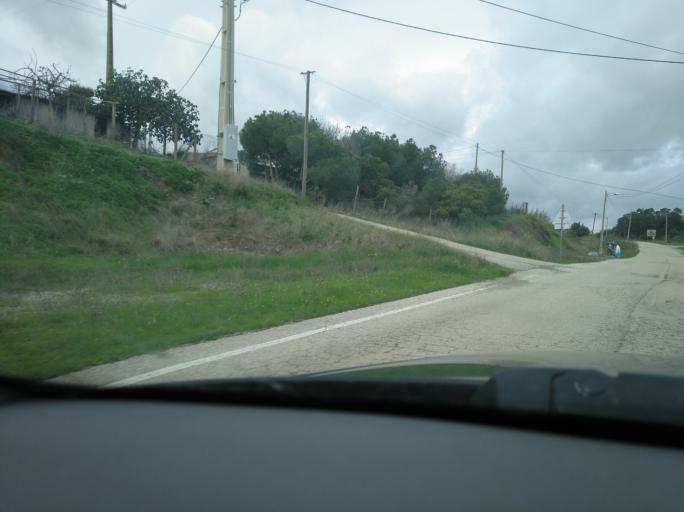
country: PT
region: Faro
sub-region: Castro Marim
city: Castro Marim
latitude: 37.2185
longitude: -7.4878
